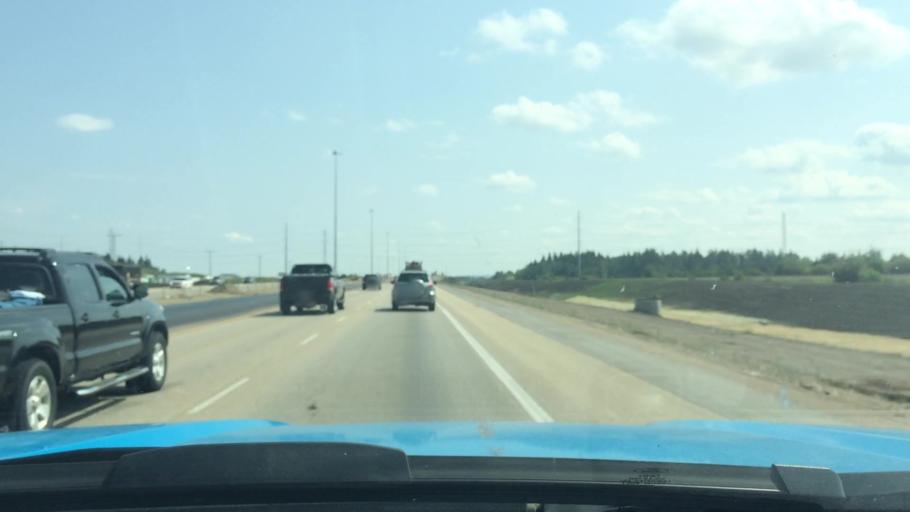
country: CA
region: Alberta
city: Red Deer
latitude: 52.2414
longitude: -113.8336
